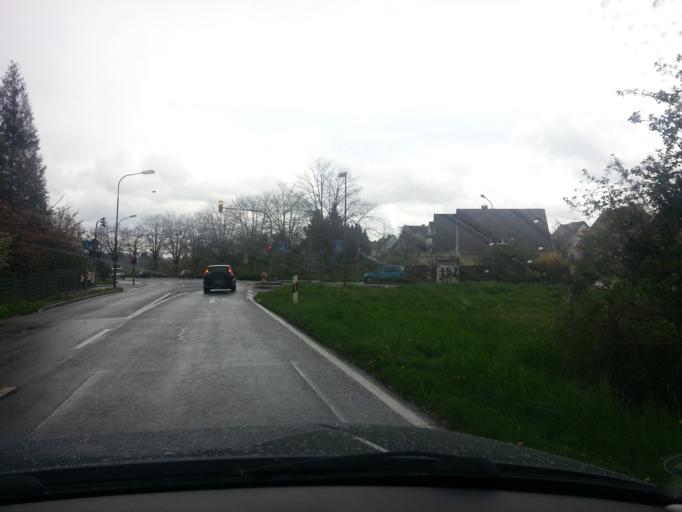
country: DE
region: Rheinland-Pfalz
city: Landau in der Pfalz
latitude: 49.1963
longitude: 8.0920
